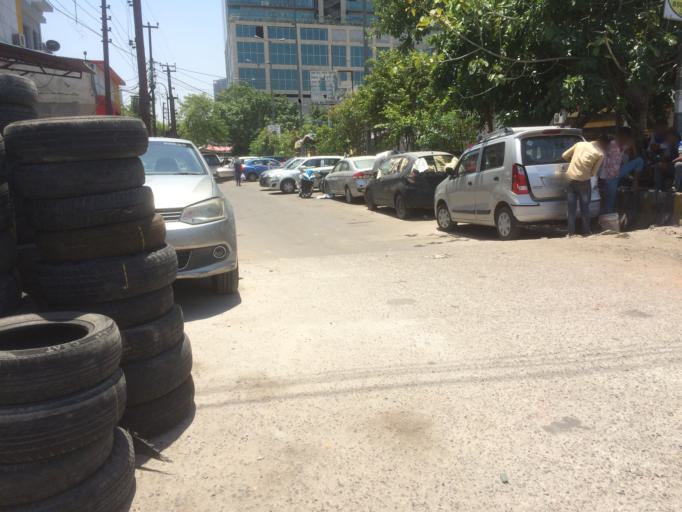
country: IN
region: Uttar Pradesh
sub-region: Gautam Buddha Nagar
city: Noida
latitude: 28.5785
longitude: 77.3163
